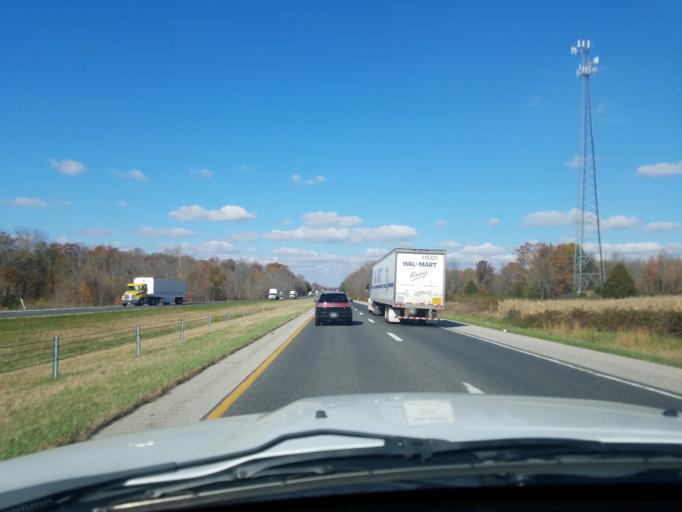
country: US
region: Indiana
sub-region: Bartholomew County
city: Columbus
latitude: 39.0935
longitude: -85.9399
